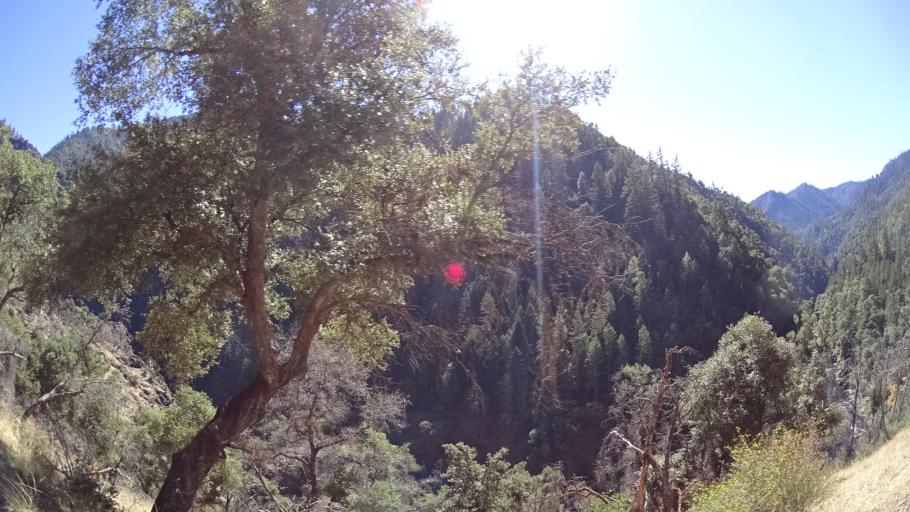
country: US
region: California
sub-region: Siskiyou County
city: Happy Camp
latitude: 41.3340
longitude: -123.3739
